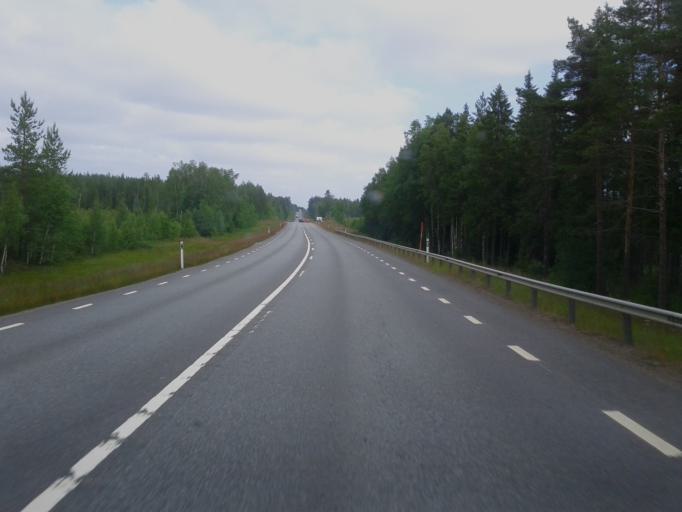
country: SE
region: Vaesterbotten
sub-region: Skelleftea Kommun
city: Burea
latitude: 64.3505
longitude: 21.2931
